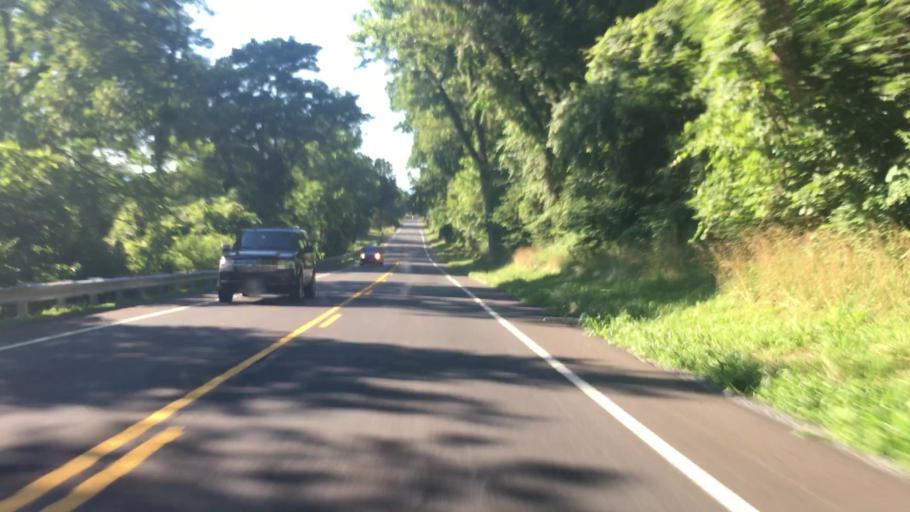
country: US
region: Maryland
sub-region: Frederick County
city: Point of Rocks
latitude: 39.2969
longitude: -77.5400
